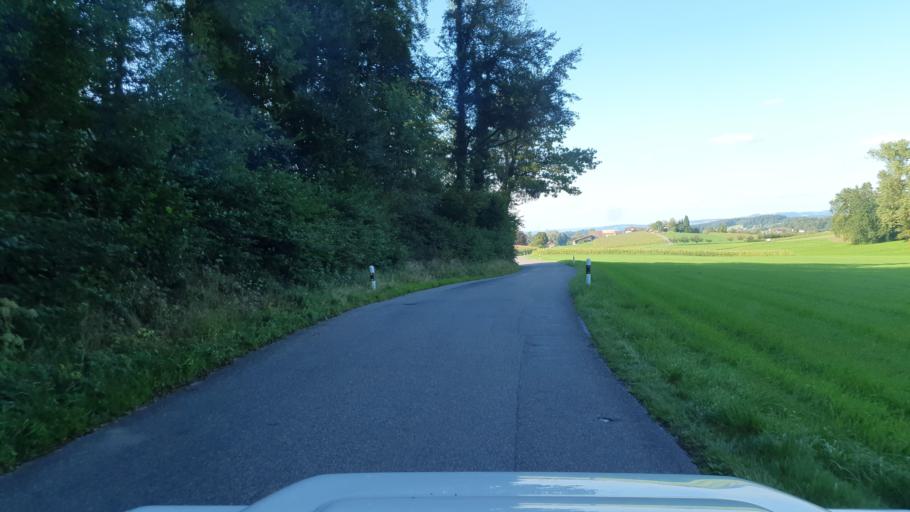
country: CH
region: Aargau
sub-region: Bezirk Muri
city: Oberruti
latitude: 47.1741
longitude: 8.3696
